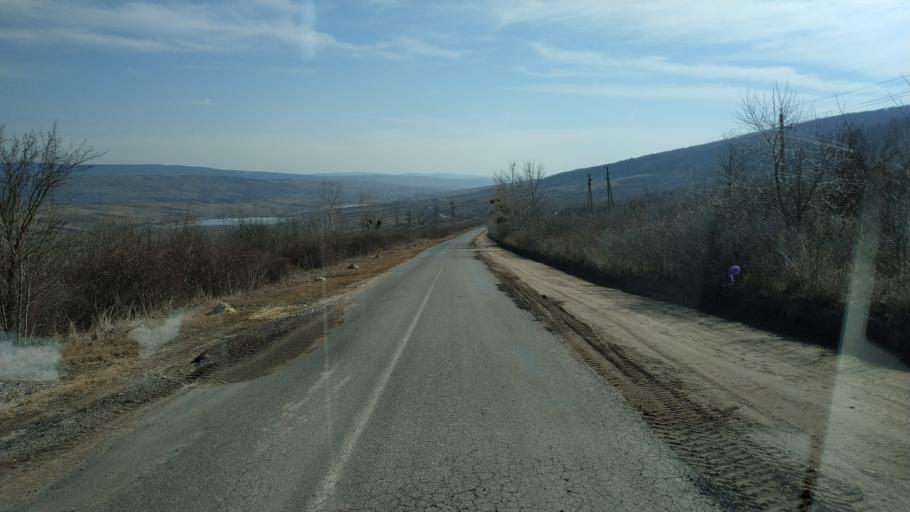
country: MD
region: Nisporeni
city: Nisporeni
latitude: 47.1897
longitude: 28.0690
